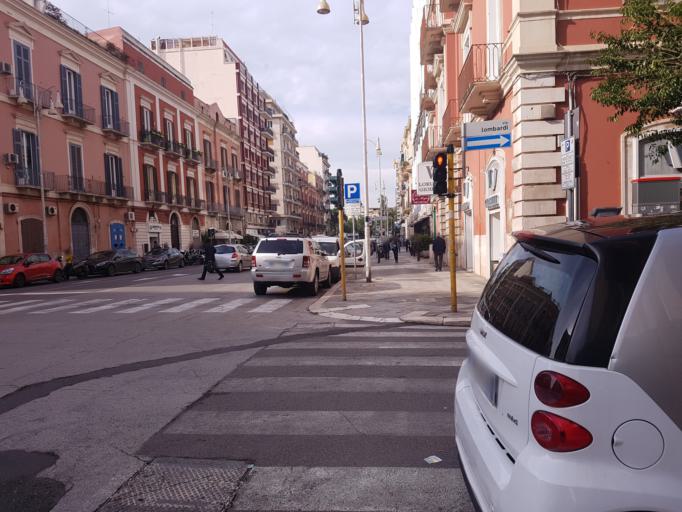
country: IT
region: Apulia
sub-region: Provincia di Bari
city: Bari
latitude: 41.1259
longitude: 16.8652
